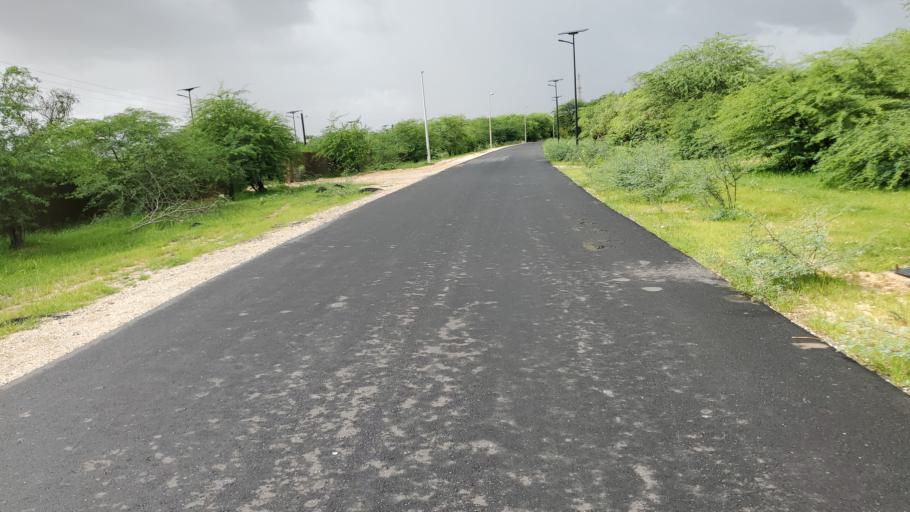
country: SN
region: Saint-Louis
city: Saint-Louis
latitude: 16.0595
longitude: -16.4281
